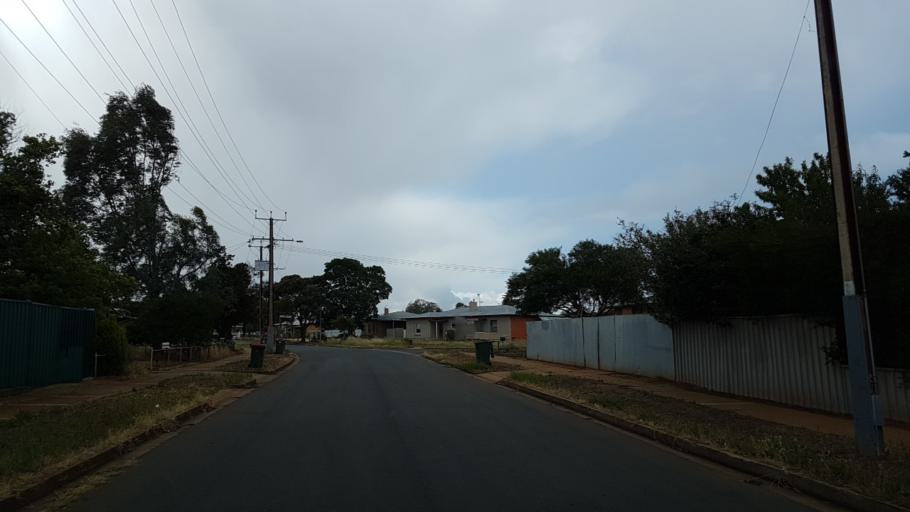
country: AU
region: South Australia
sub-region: Playford
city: Smithfield
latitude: -34.6923
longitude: 138.6639
